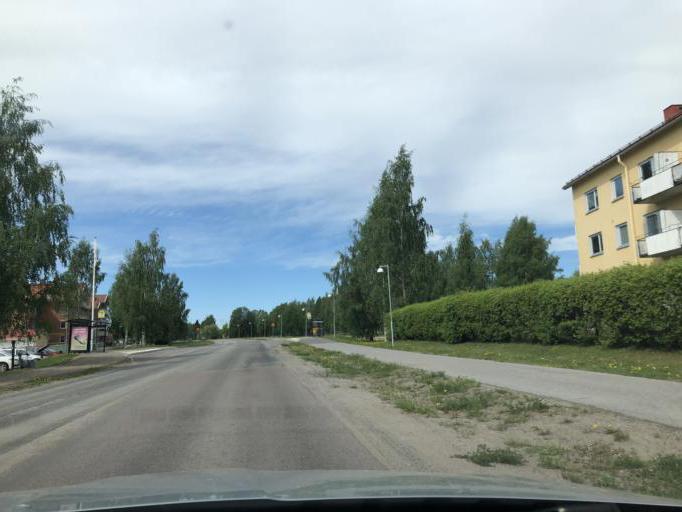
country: SE
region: Norrbotten
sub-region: Pitea Kommun
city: Pitea
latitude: 65.3223
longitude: 21.4668
